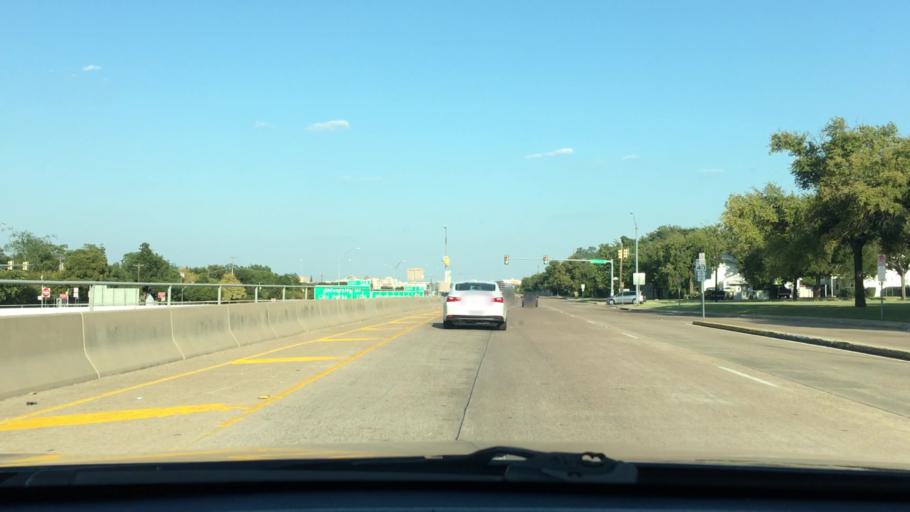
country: US
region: Texas
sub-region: Tarrant County
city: Westworth
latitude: 32.7326
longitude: -97.3852
